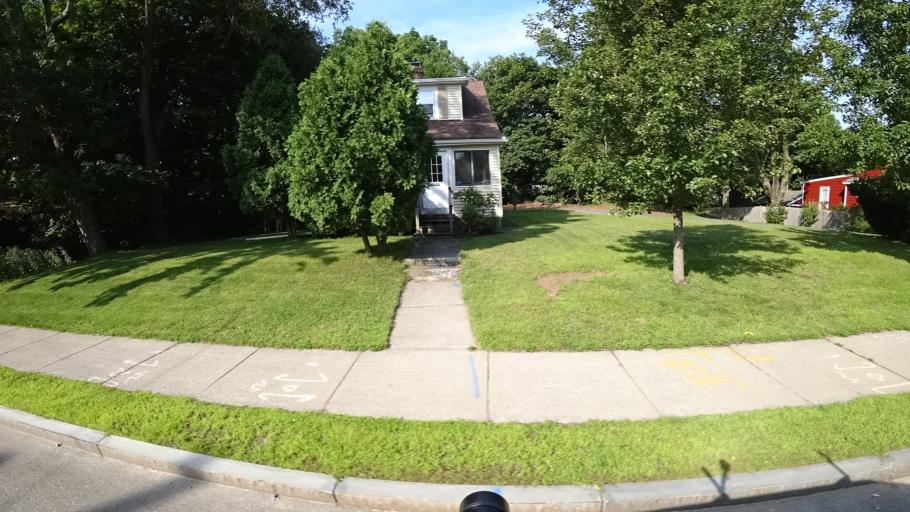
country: US
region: Massachusetts
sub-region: Norfolk County
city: Dedham
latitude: 42.2330
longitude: -71.1607
